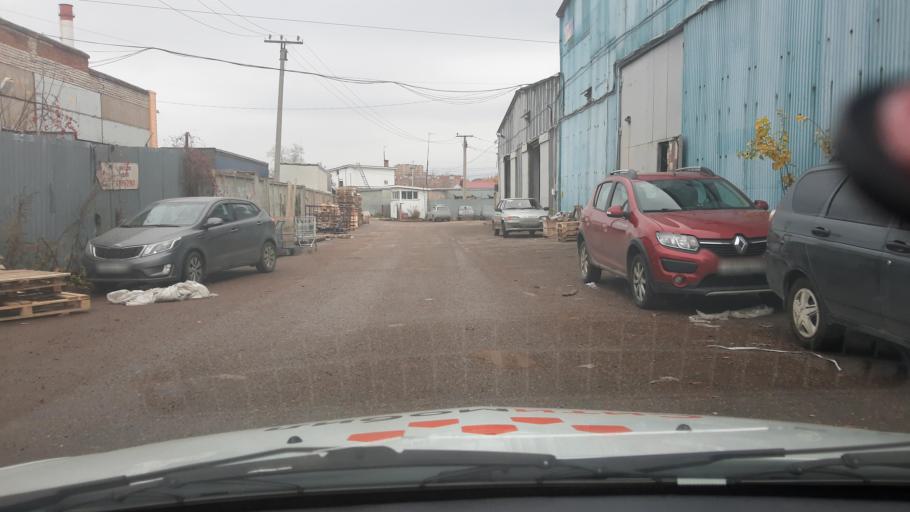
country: RU
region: Bashkortostan
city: Ufa
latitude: 54.7837
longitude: 56.0646
